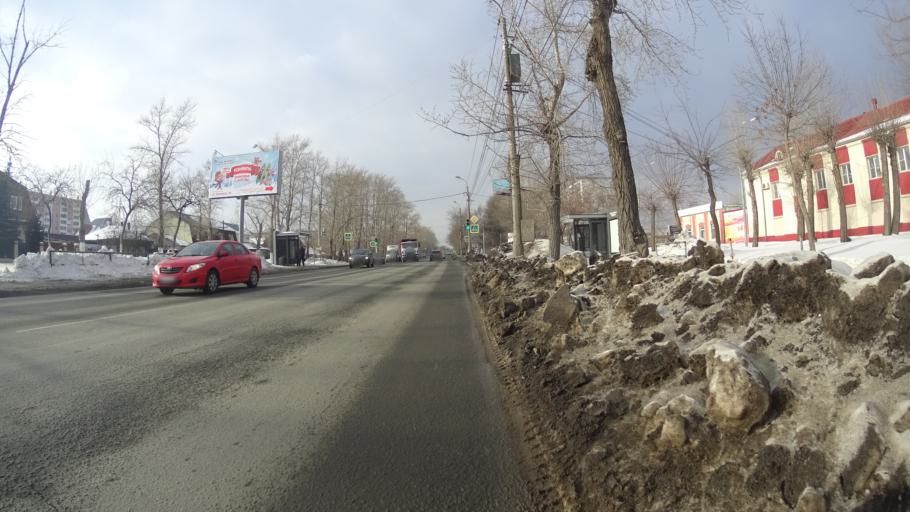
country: RU
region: Chelyabinsk
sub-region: Gorod Chelyabinsk
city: Chelyabinsk
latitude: 55.1237
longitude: 61.3736
